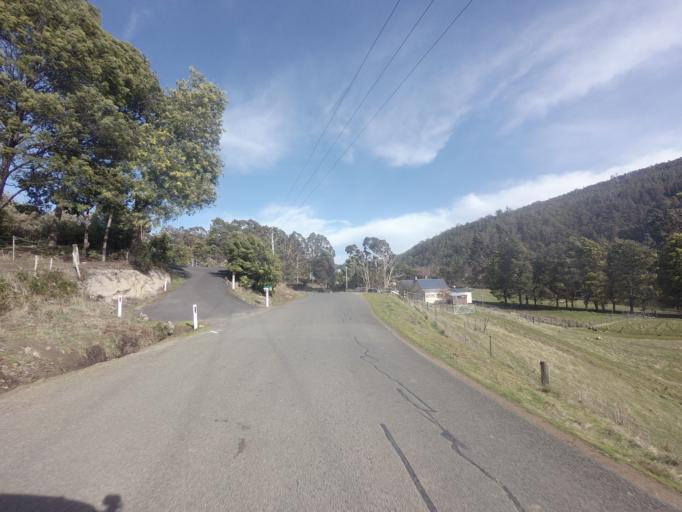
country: AU
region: Tasmania
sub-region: Huon Valley
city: Huonville
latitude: -43.0461
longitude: 147.1156
